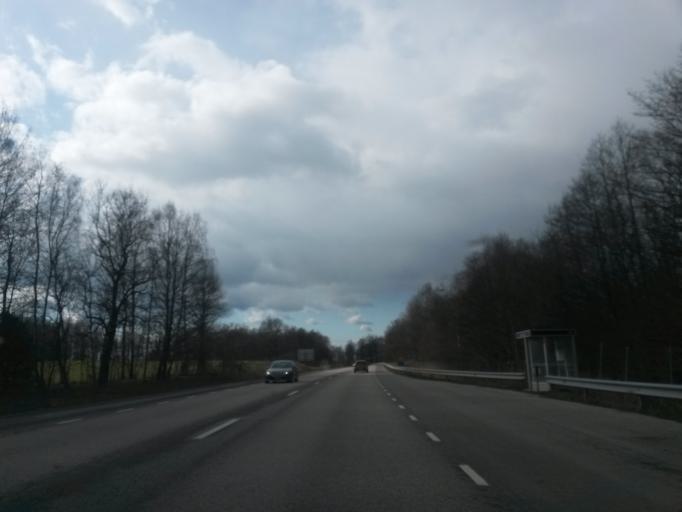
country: SE
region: Vaestra Goetaland
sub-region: Skara Kommun
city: Axvall
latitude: 58.3807
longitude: 13.6838
